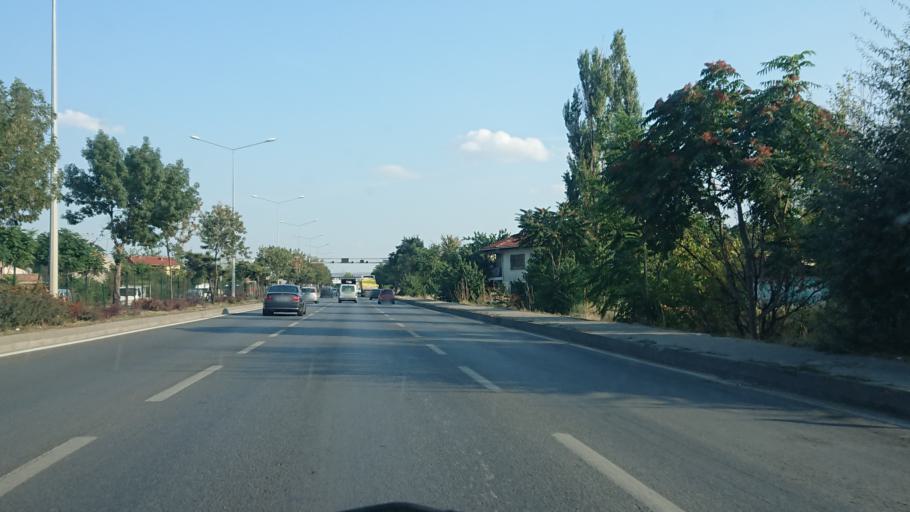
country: TR
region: Eskisehir
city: Eskisehir
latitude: 39.7667
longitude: 30.5644
